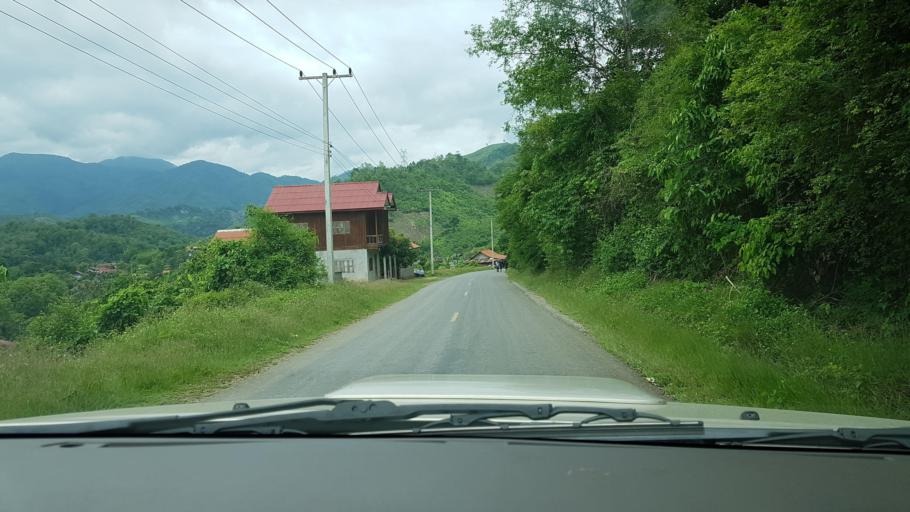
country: TH
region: Nan
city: Chaloem Phra Kiat
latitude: 19.9679
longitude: 101.2670
